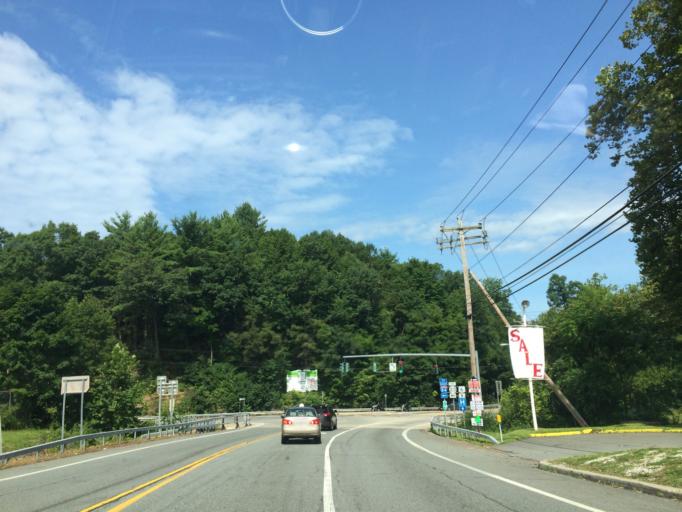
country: US
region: New York
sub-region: Orange County
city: Port Jervis
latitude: 41.3564
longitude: -74.6812
